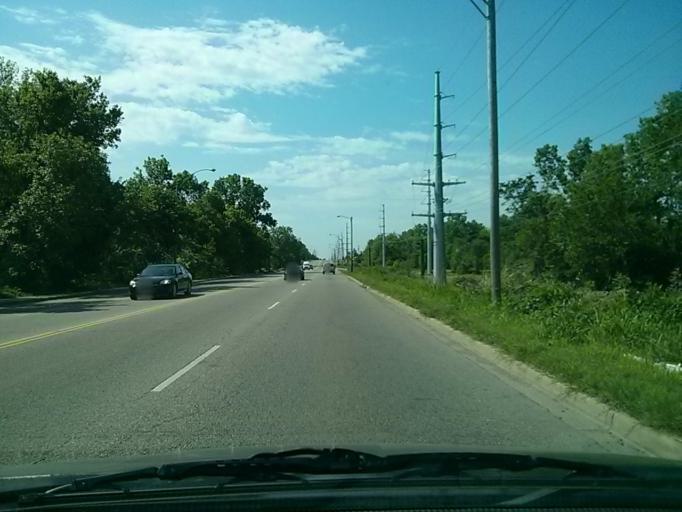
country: US
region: Oklahoma
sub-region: Tulsa County
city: Turley
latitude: 36.2152
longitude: -95.9757
